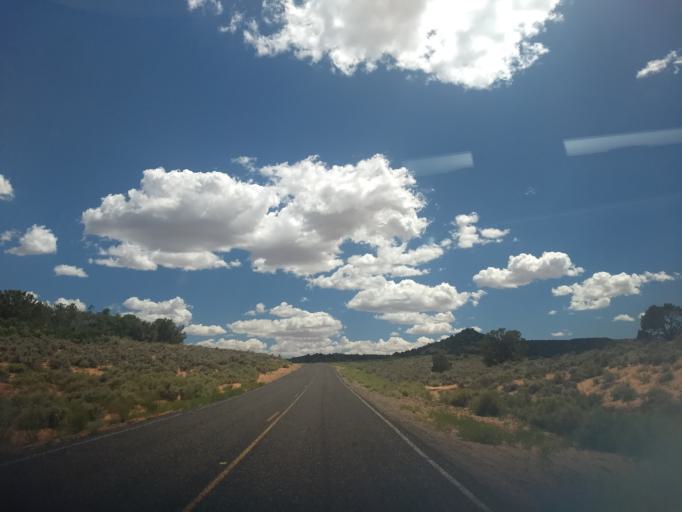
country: US
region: Utah
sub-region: Kane County
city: Kanab
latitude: 37.1403
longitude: -112.6756
